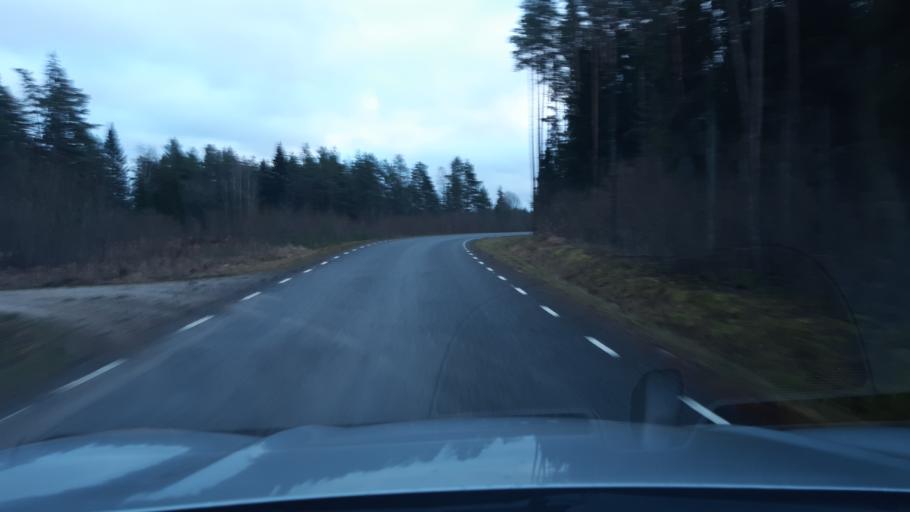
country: EE
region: Harju
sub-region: Saku vald
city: Saku
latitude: 59.1774
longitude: 24.6198
